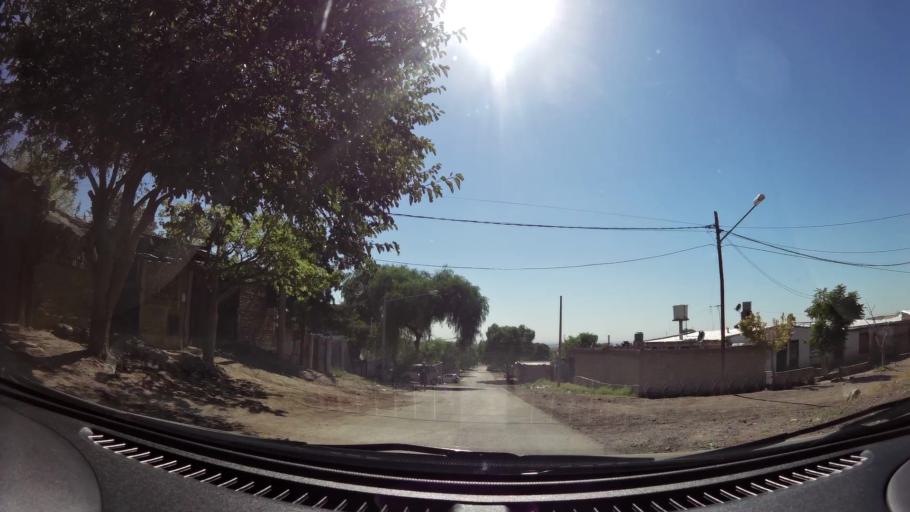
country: AR
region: Mendoza
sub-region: Departamento de Godoy Cruz
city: Godoy Cruz
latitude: -32.9122
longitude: -68.8842
